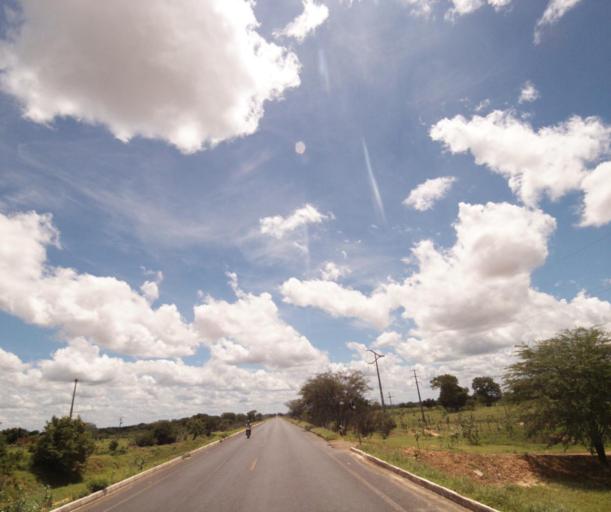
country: BR
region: Bahia
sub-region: Bom Jesus Da Lapa
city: Bom Jesus da Lapa
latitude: -13.2576
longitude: -43.4654
